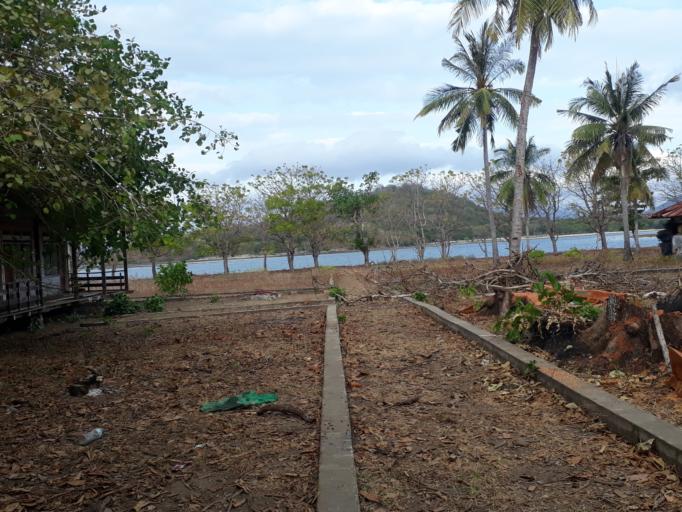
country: ID
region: West Nusa Tenggara
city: Tawun
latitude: -8.7444
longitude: 115.8899
